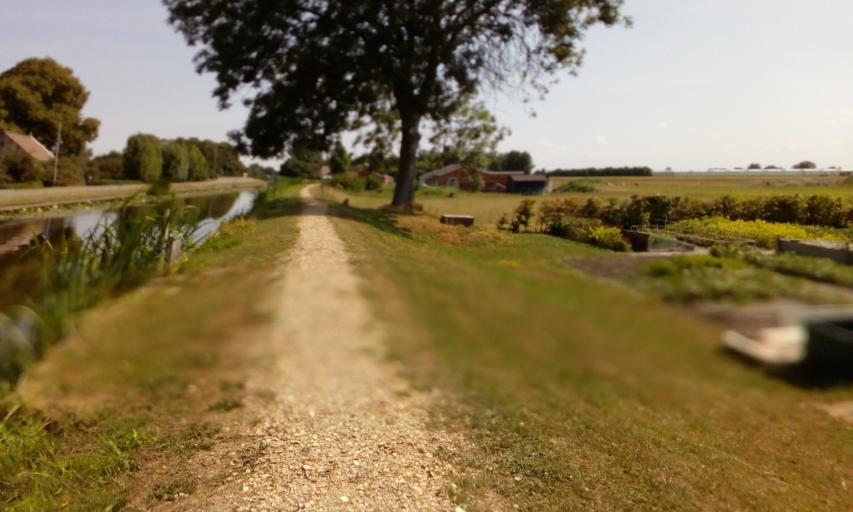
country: NL
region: South Holland
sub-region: Gemeente Westland
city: De Lier
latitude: 51.9520
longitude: 4.2827
